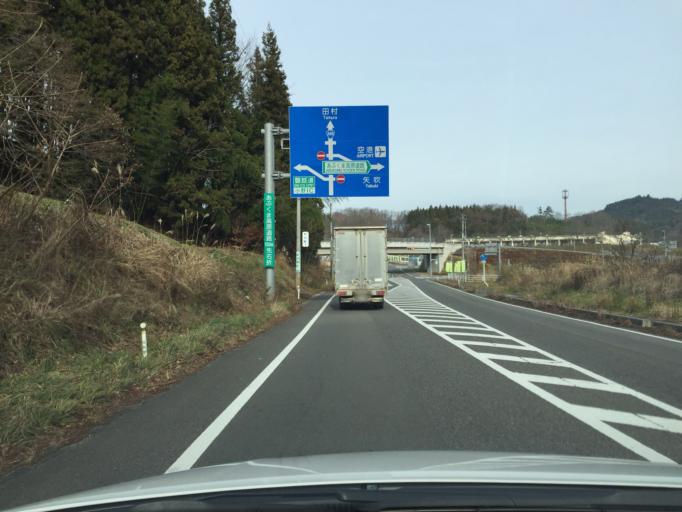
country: JP
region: Fukushima
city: Funehikimachi-funehiki
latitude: 37.2897
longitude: 140.6171
